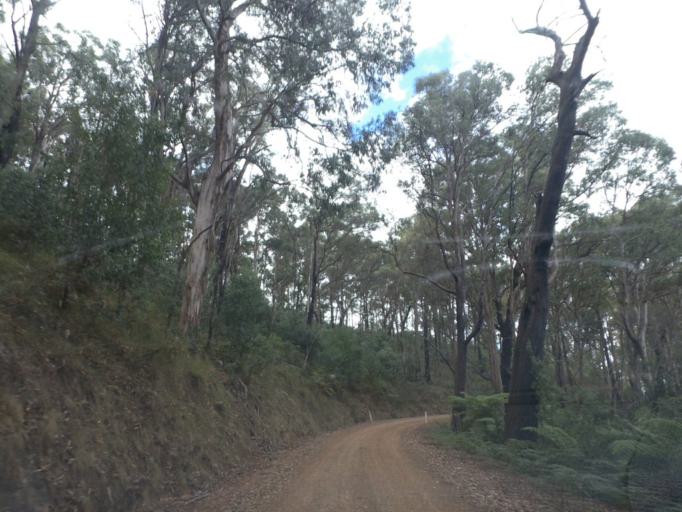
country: AU
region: Victoria
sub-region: Murrindindi
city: Alexandra
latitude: -37.4289
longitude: 145.9740
